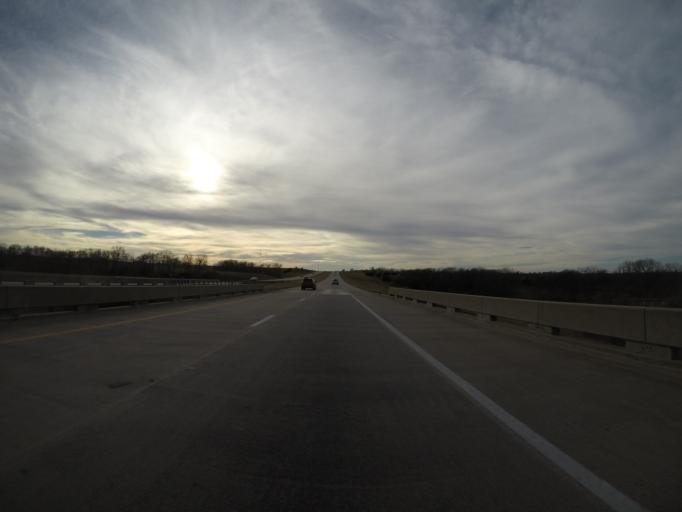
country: US
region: Kansas
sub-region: Franklin County
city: Ottawa
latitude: 38.4983
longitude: -95.4527
